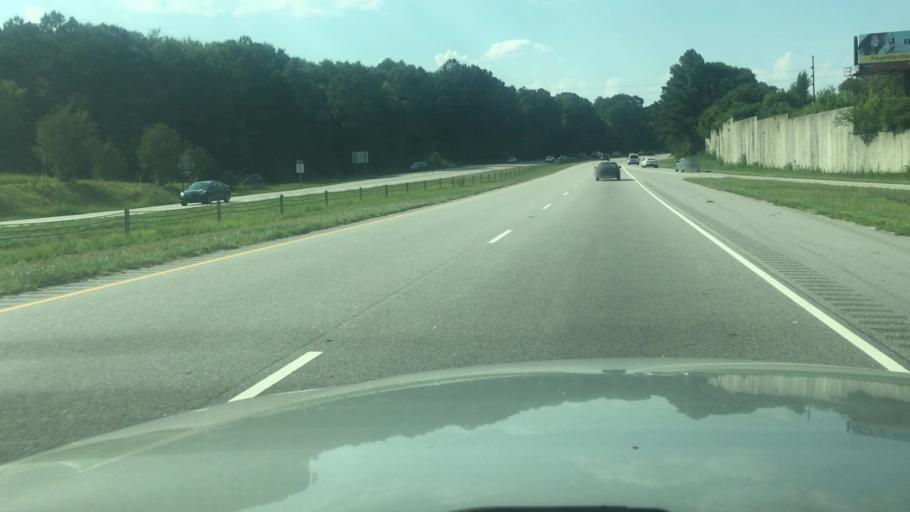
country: US
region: North Carolina
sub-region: Cumberland County
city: Fayetteville
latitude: 35.0466
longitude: -78.8933
